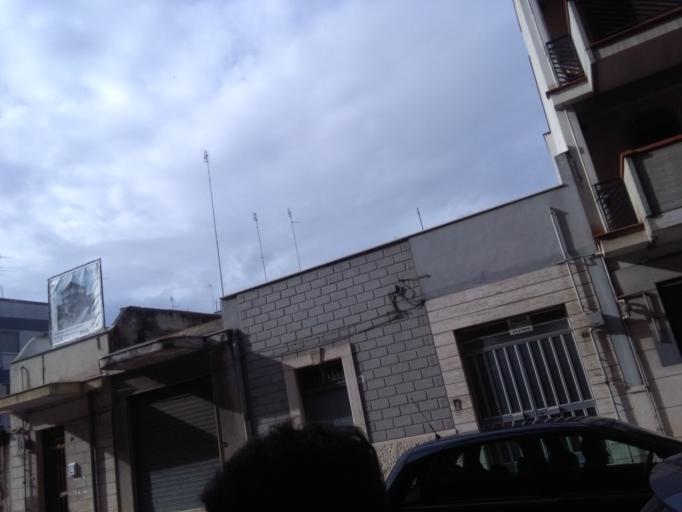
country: IT
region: Apulia
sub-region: Provincia di Barletta - Andria - Trani
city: Andria
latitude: 41.2344
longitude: 16.2946
